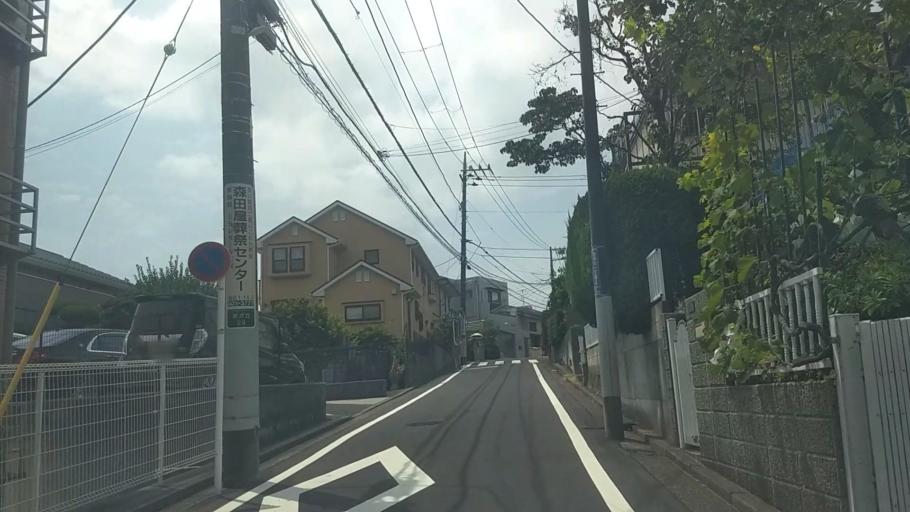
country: JP
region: Kanagawa
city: Yokohama
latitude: 35.5079
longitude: 139.6297
